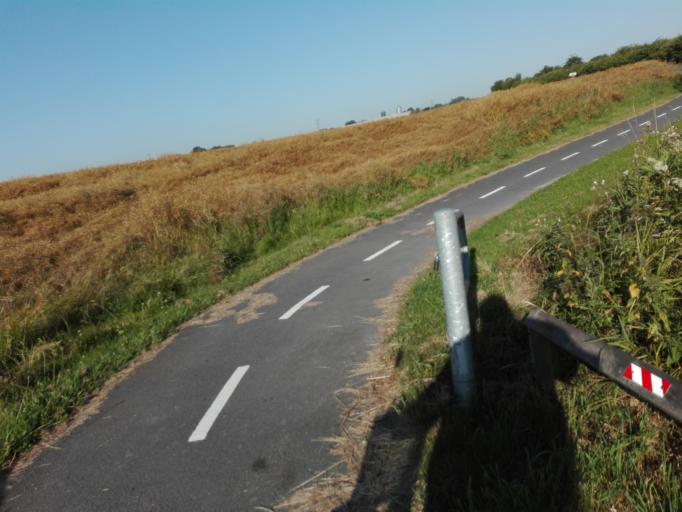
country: DK
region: Central Jutland
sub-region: Arhus Kommune
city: Marslet
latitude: 56.0682
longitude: 10.1528
